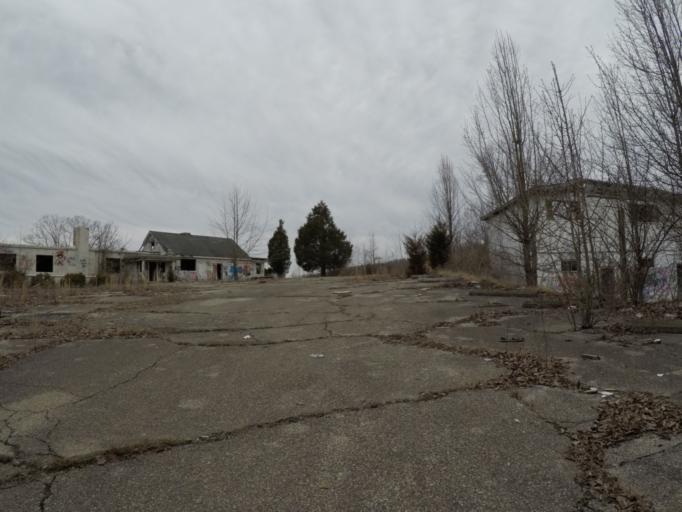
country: US
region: Ohio
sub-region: Lawrence County
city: Burlington
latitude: 38.3835
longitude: -82.5098
